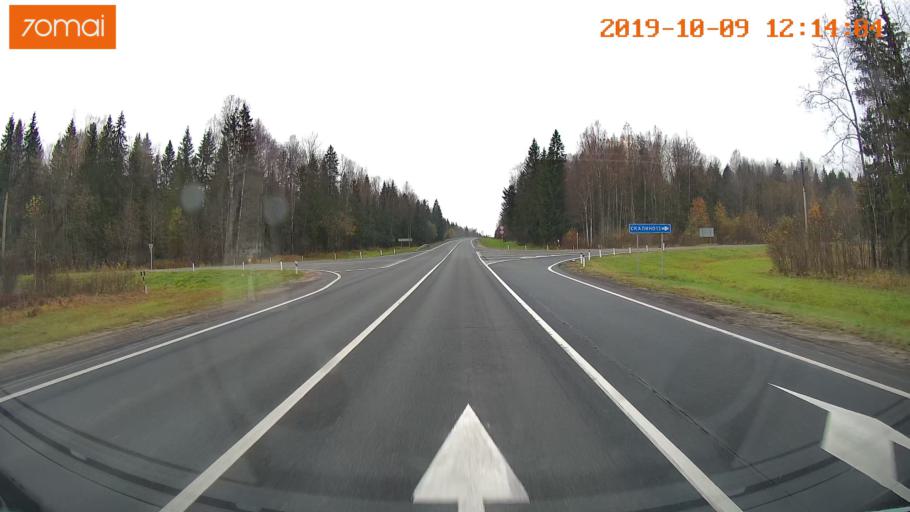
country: RU
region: Jaroslavl
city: Prechistoye
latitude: 58.5010
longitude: 40.3411
